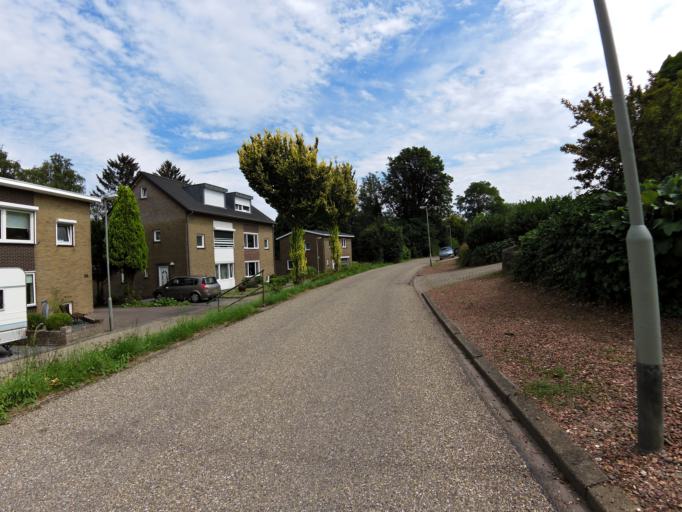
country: NL
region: Limburg
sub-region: Valkenburg aan de Geul
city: Schin op Geul
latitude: 50.8164
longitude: 5.9005
